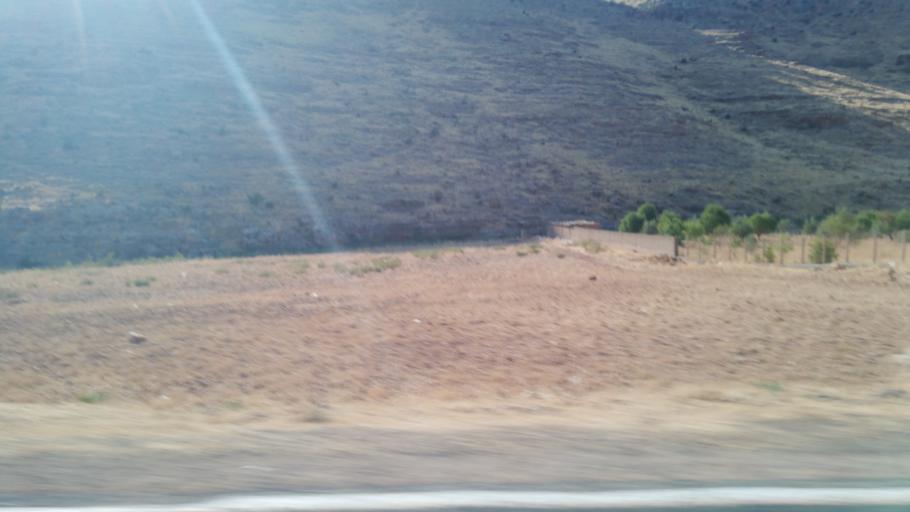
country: TR
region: Mardin
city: Sivrice
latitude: 37.2338
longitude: 41.3327
